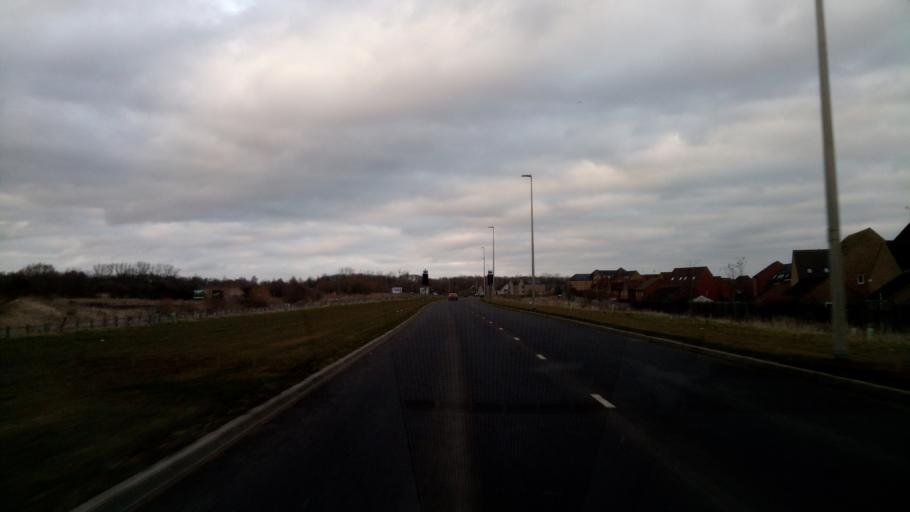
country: GB
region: England
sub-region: Cambridgeshire
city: Yaxley
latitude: 52.5352
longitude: -0.2831
